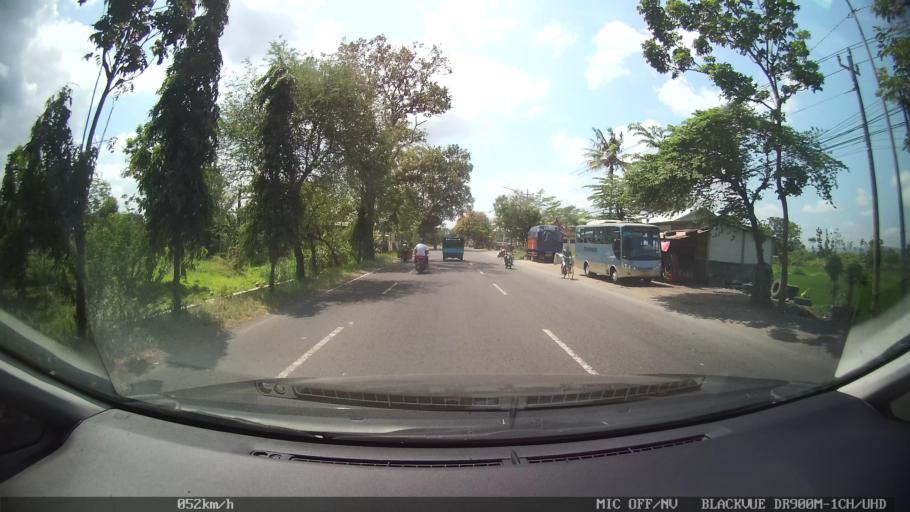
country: ID
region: Daerah Istimewa Yogyakarta
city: Pandak
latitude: -7.9092
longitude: 110.2985
